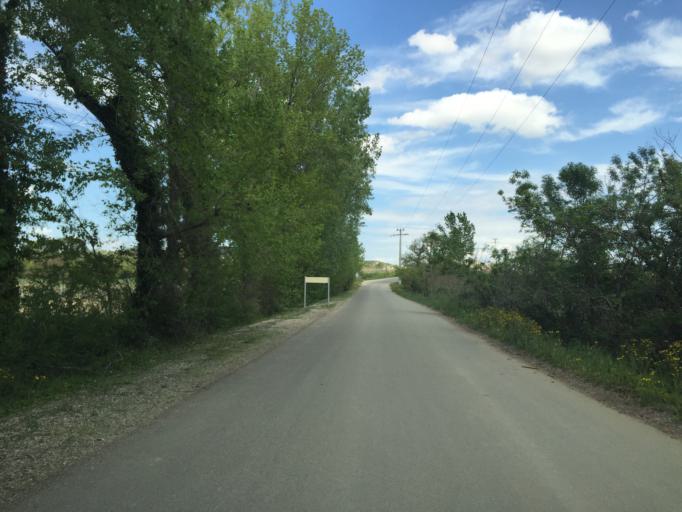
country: FR
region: Provence-Alpes-Cote d'Azur
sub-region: Departement du Vaucluse
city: Chateauneuf-du-Pape
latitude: 44.0422
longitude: 4.8256
